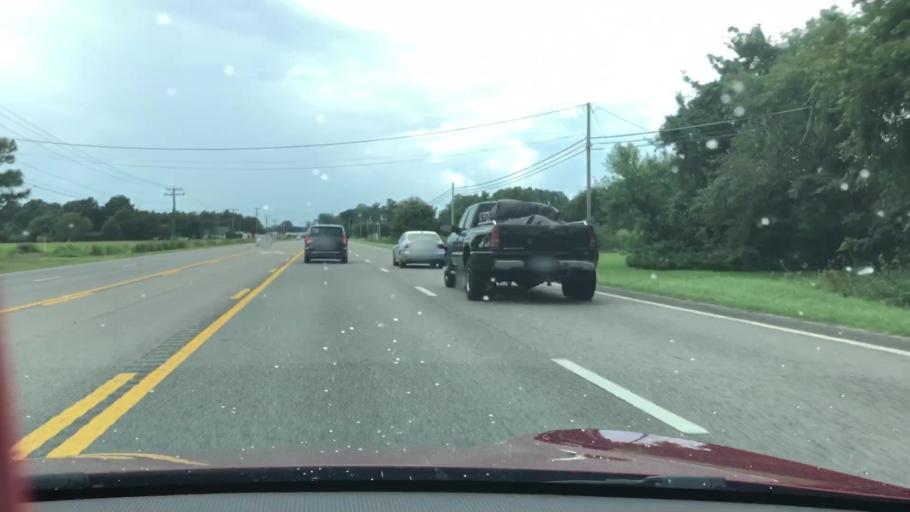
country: US
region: North Carolina
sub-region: Dare County
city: Southern Shores
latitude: 36.1340
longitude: -75.8389
